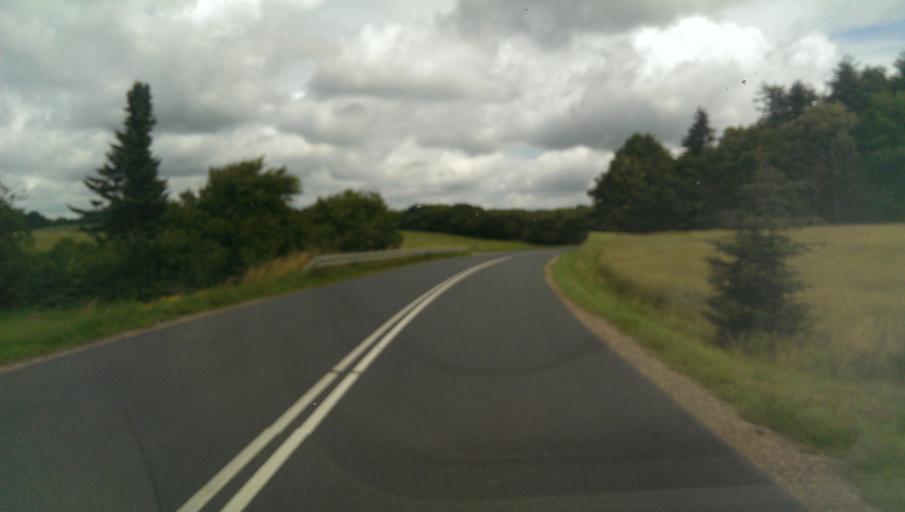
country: DK
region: Central Jutland
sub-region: Silkeborg Kommune
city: Virklund
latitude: 56.0915
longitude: 9.5246
